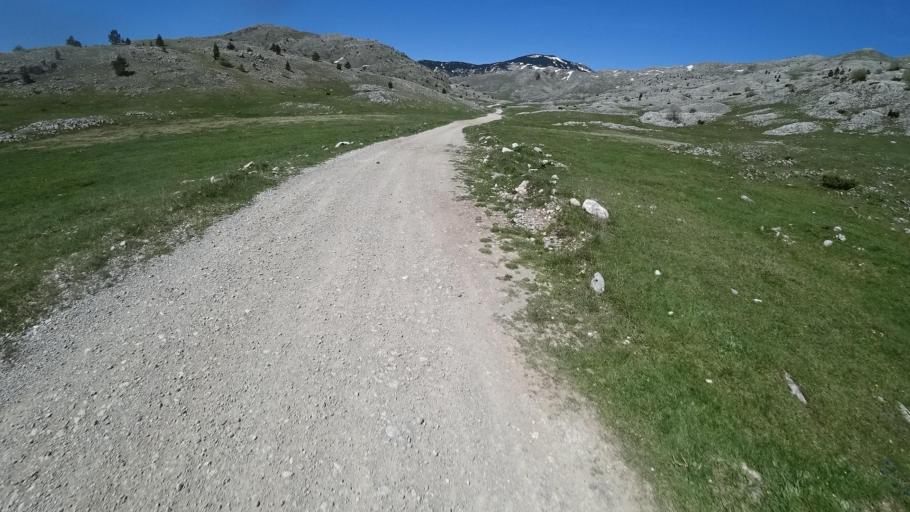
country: BA
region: Federation of Bosnia and Herzegovina
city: Gracanica
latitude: 43.6862
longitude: 18.2200
